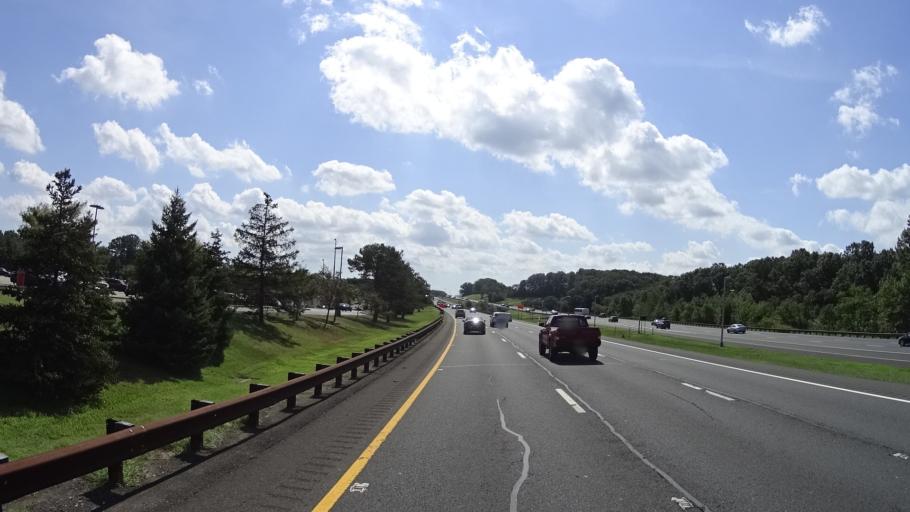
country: US
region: New Jersey
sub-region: Middlesex County
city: South Amboy
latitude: 40.4653
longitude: -74.2892
